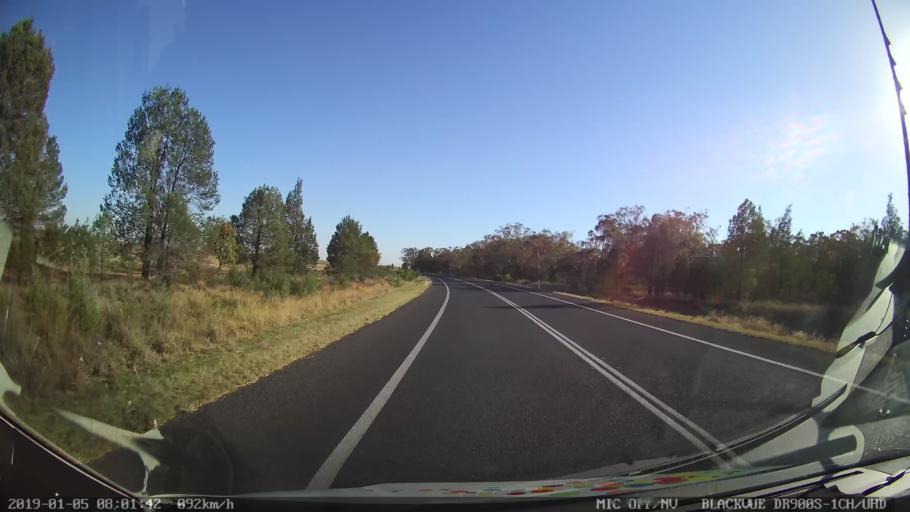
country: AU
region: New South Wales
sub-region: Gilgandra
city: Gilgandra
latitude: -31.6845
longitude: 148.7059
